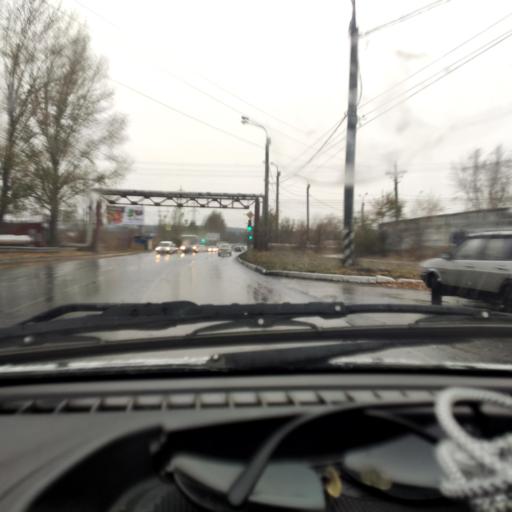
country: RU
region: Samara
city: Zhigulevsk
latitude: 53.4860
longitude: 49.5098
